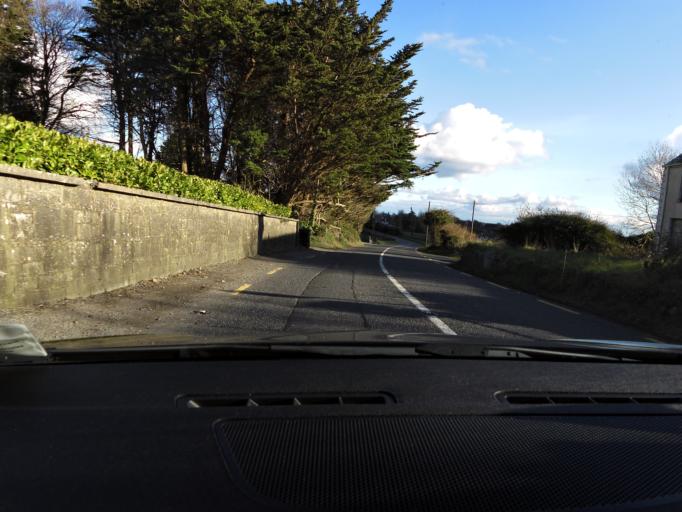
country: IE
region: Connaught
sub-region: Roscommon
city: Roscommon
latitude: 53.6736
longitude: -8.3409
